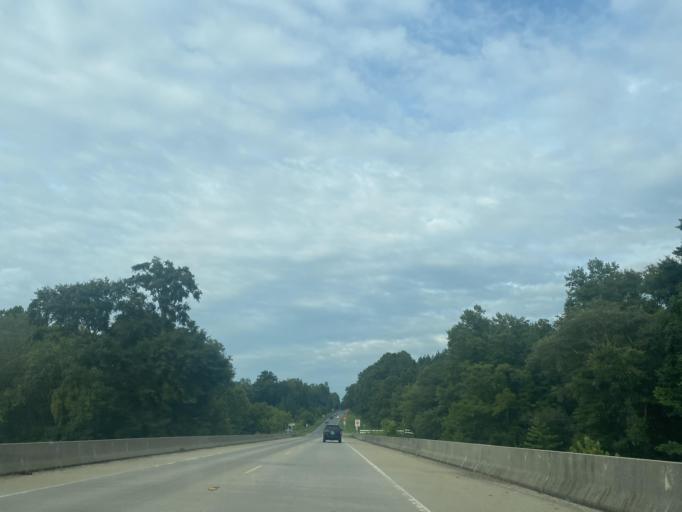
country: US
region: South Carolina
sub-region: Cherokee County
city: East Gaffney
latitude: 35.0890
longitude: -81.5714
